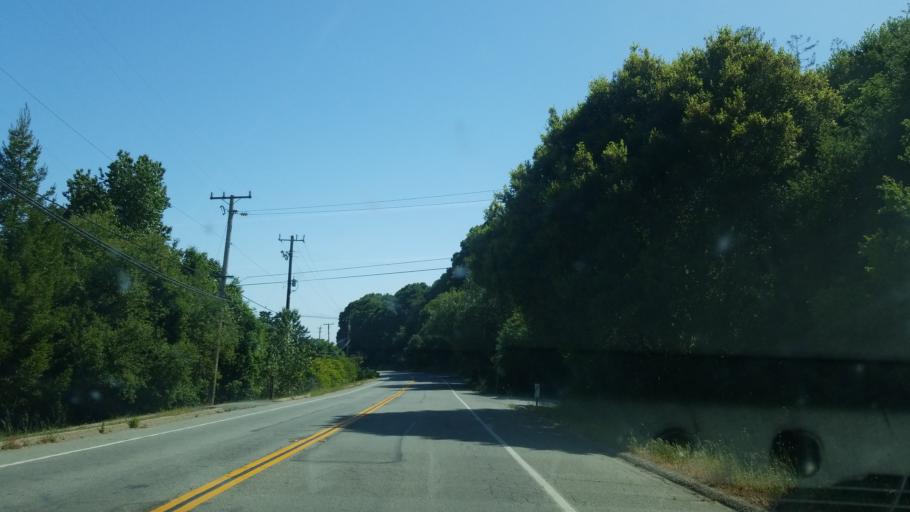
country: US
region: California
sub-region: Santa Cruz County
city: Soquel
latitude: 37.0224
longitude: -121.9516
